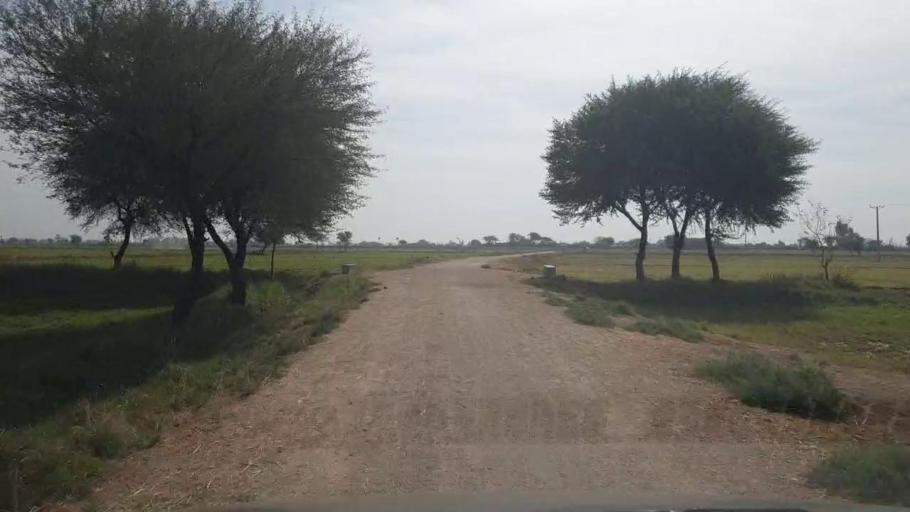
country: PK
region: Sindh
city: Umarkot
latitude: 25.3567
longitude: 69.6051
